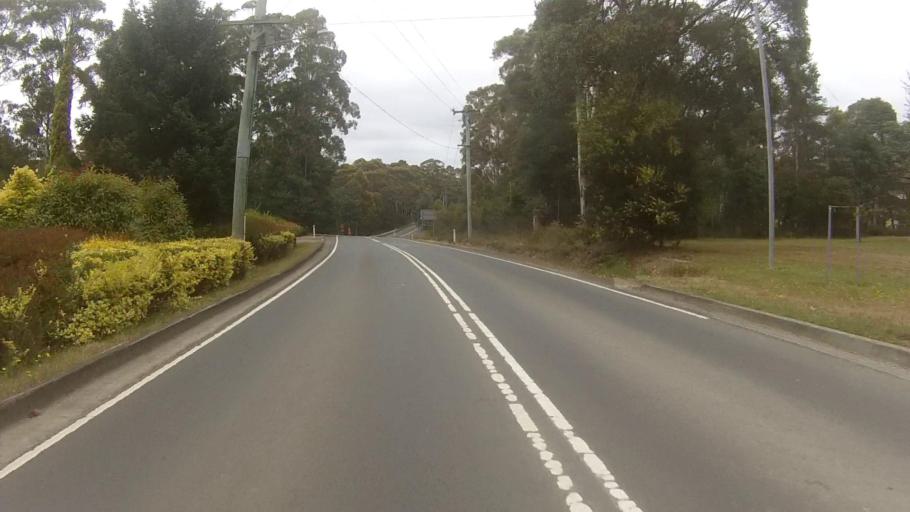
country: AU
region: Tasmania
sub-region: Kingborough
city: Margate
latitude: -42.9850
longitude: 147.1960
